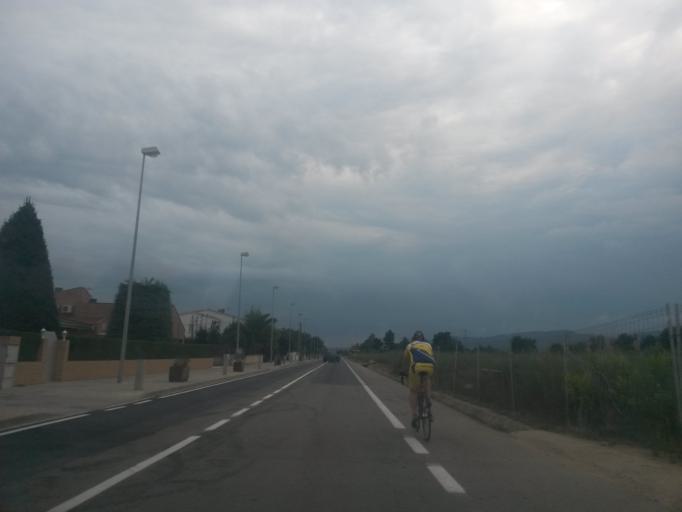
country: ES
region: Catalonia
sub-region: Provincia de Girona
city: Banyoles
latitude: 42.1465
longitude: 2.7697
